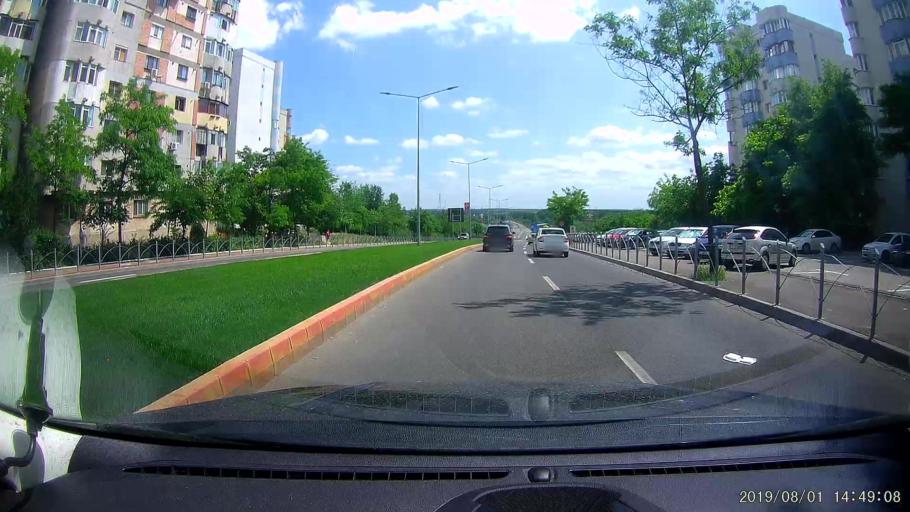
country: RO
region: Galati
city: Galati
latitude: 45.4087
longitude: 28.0151
